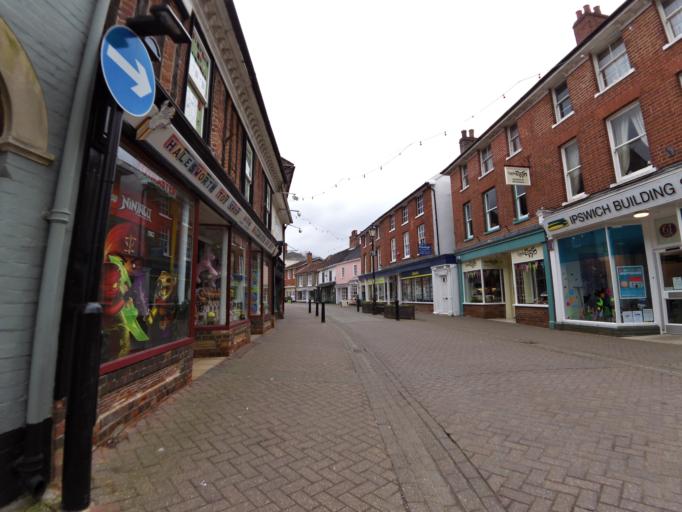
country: GB
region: England
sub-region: Suffolk
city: Halesworth
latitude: 52.3443
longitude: 1.5019
